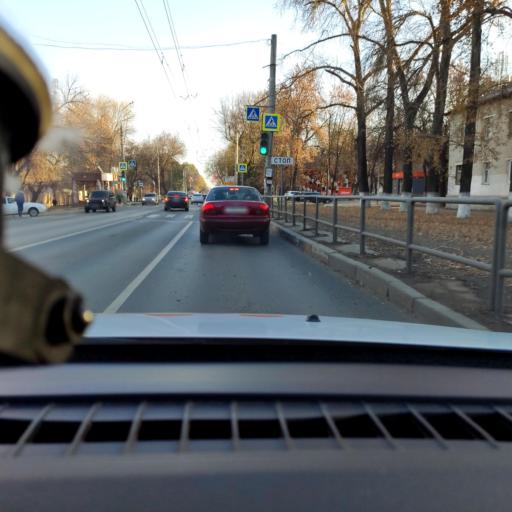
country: RU
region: Samara
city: Samara
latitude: 53.2372
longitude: 50.2400
